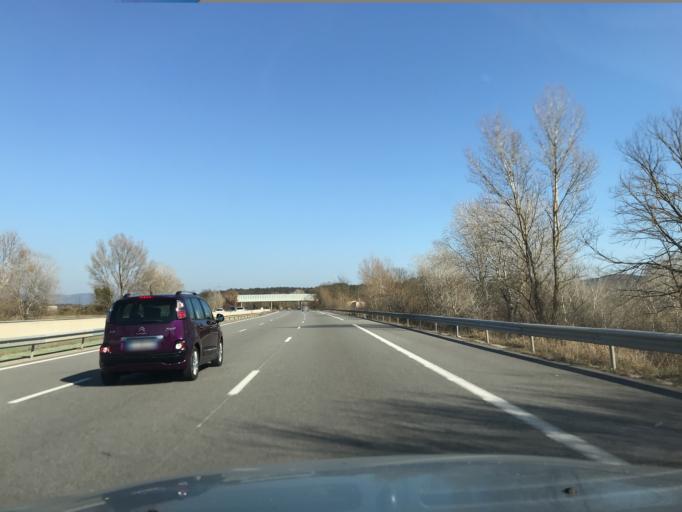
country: FR
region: Provence-Alpes-Cote d'Azur
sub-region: Departement du Var
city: Les Arcs
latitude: 43.4425
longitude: 6.4847
